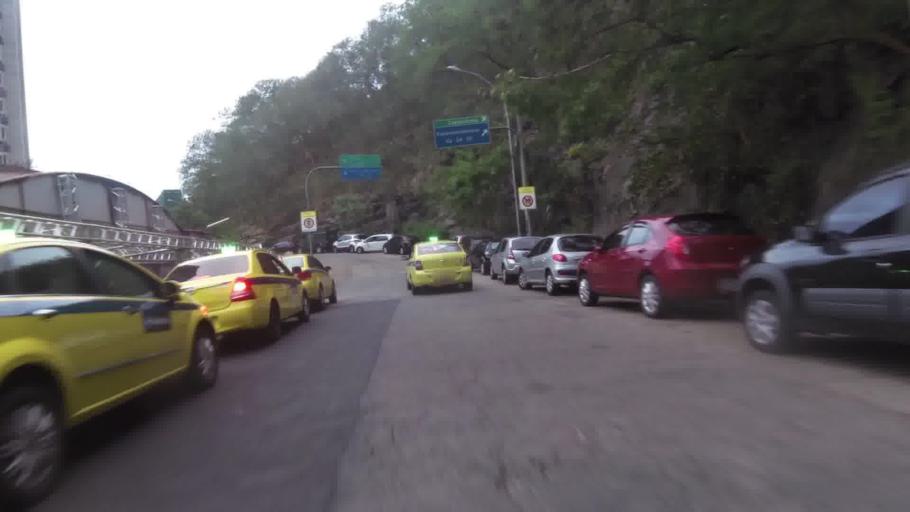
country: BR
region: Rio de Janeiro
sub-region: Rio De Janeiro
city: Rio de Janeiro
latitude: -22.9589
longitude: -43.1768
